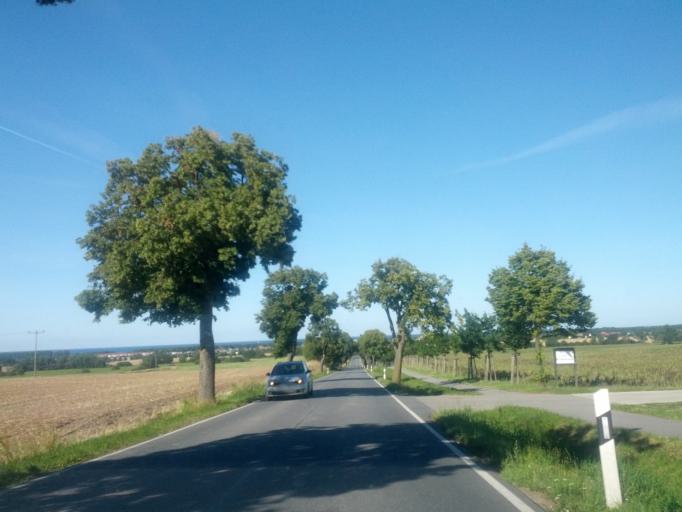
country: DE
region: Mecklenburg-Vorpommern
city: Bastorf
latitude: 54.1329
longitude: 11.7057
